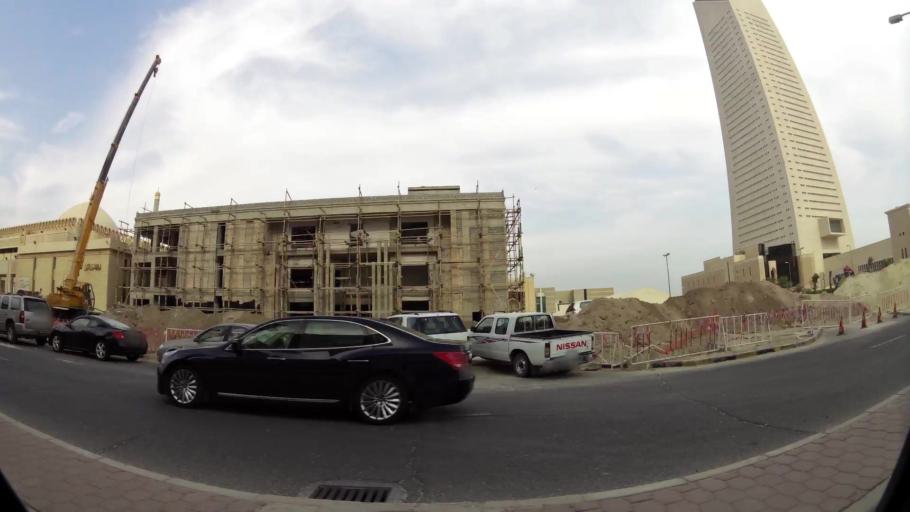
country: KW
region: Al Asimah
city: Kuwait City
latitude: 29.3793
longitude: 47.9768
